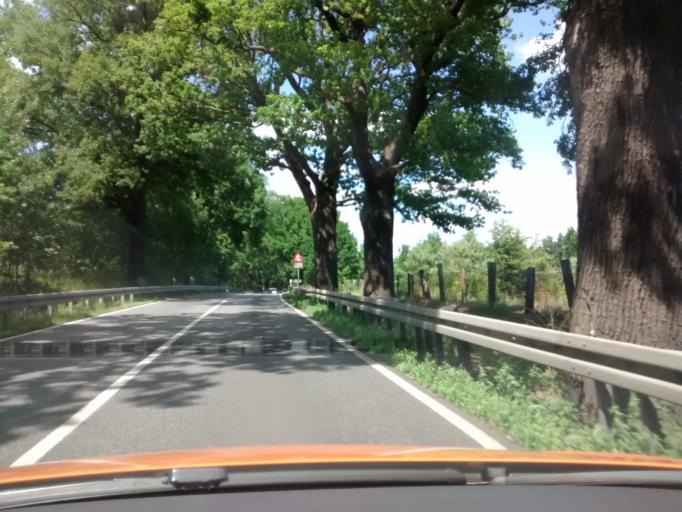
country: DE
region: Brandenburg
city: Potsdam
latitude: 52.4534
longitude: 13.0468
